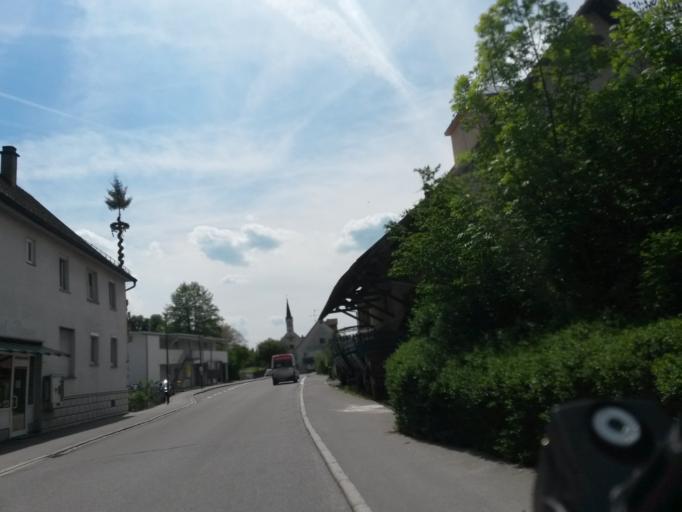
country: DE
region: Baden-Wuerttemberg
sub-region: Tuebingen Region
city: Bad Waldsee
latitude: 47.9216
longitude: 9.7376
